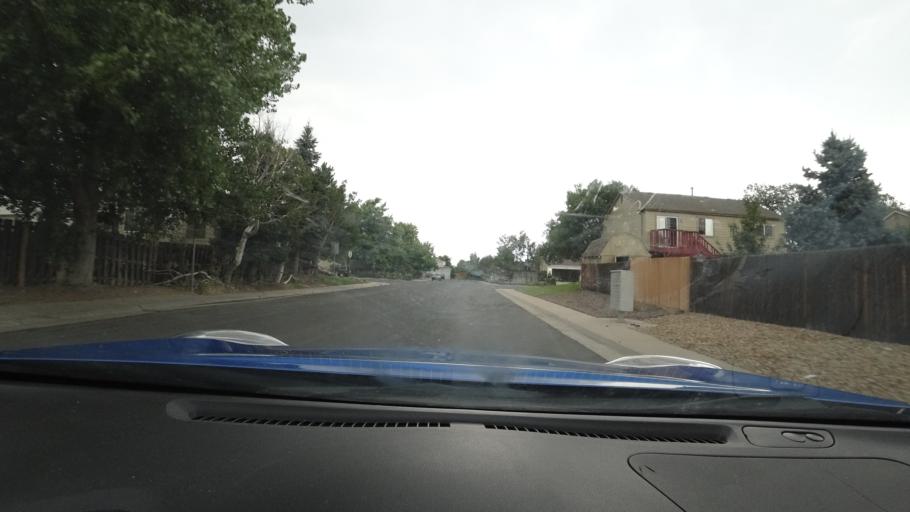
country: US
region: Colorado
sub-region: Adams County
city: Aurora
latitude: 39.7749
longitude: -104.7482
